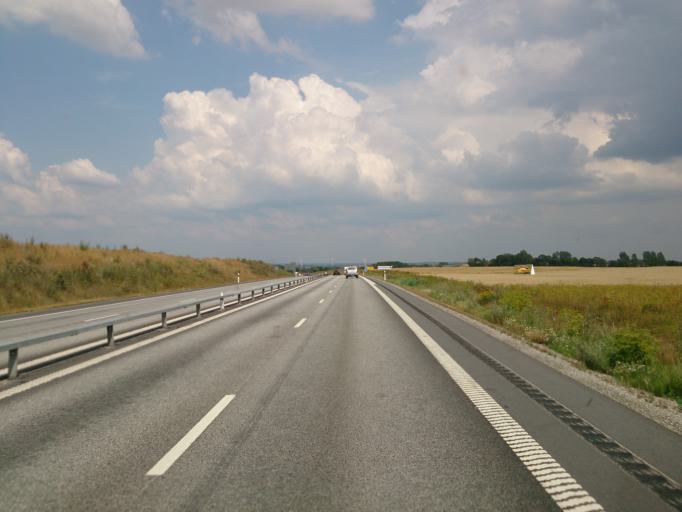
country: SE
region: Skane
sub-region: Hoors Kommun
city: Loberod
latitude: 55.7888
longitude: 13.4346
